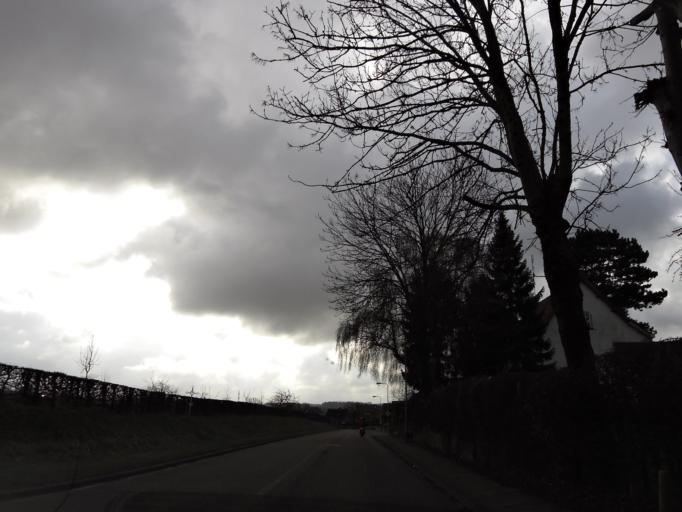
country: NL
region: Limburg
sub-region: Eijsden-Margraten
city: Eijsden
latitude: 50.7987
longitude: 5.7639
